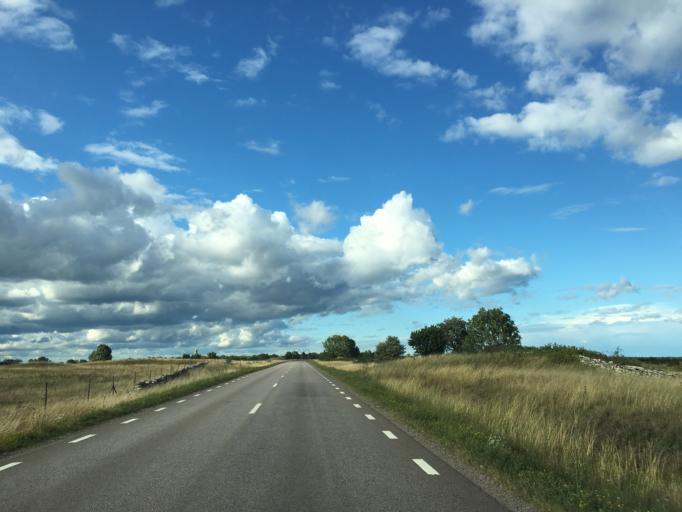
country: SE
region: Kalmar
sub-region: Morbylanga Kommun
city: Moerbylanga
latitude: 56.5303
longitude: 16.4422
